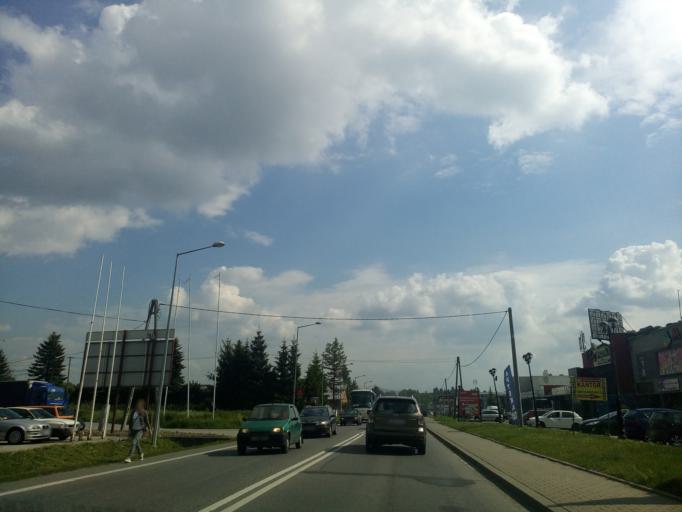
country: PL
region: Lesser Poland Voivodeship
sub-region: Powiat nowosadecki
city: Nowy Sacz
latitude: 49.6571
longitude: 20.6896
